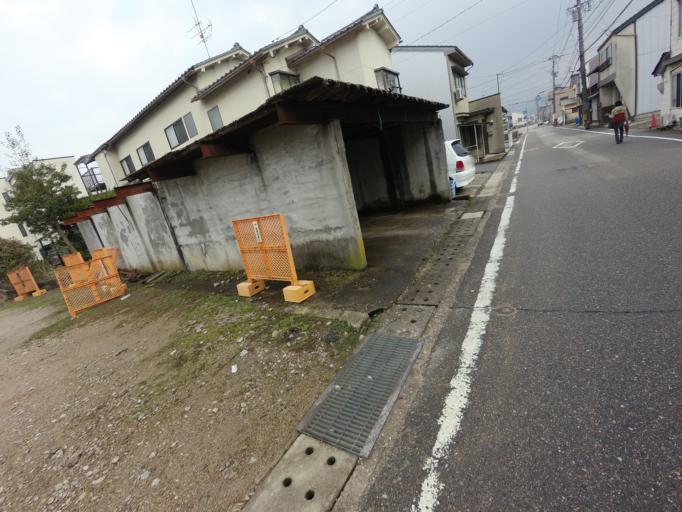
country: JP
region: Ishikawa
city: Nanao
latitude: 37.0475
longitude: 136.9648
